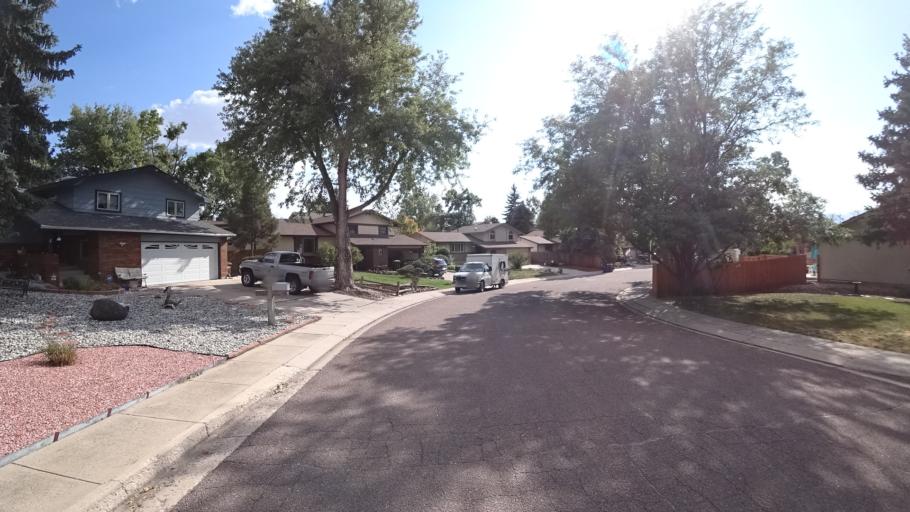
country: US
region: Colorado
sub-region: El Paso County
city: Cimarron Hills
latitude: 38.8725
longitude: -104.7348
